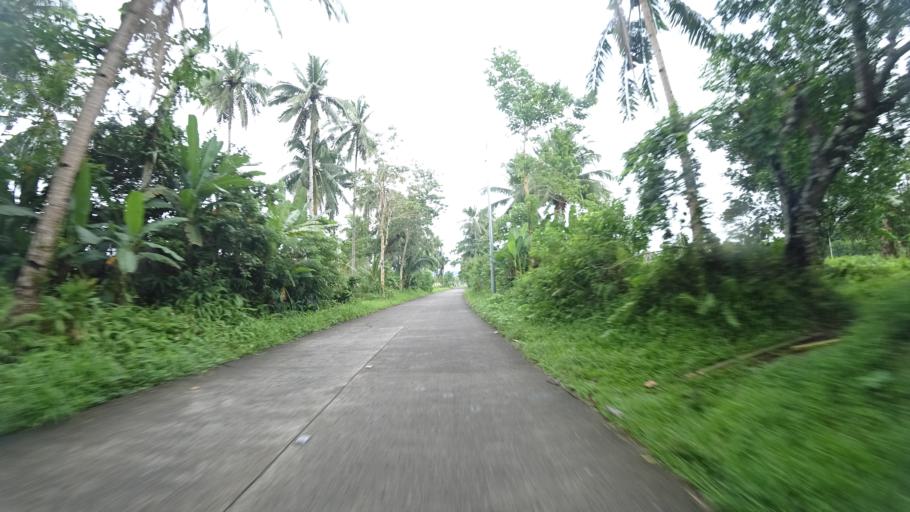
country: PH
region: Eastern Visayas
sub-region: Province of Leyte
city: Bugho
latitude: 10.8208
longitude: 124.9414
